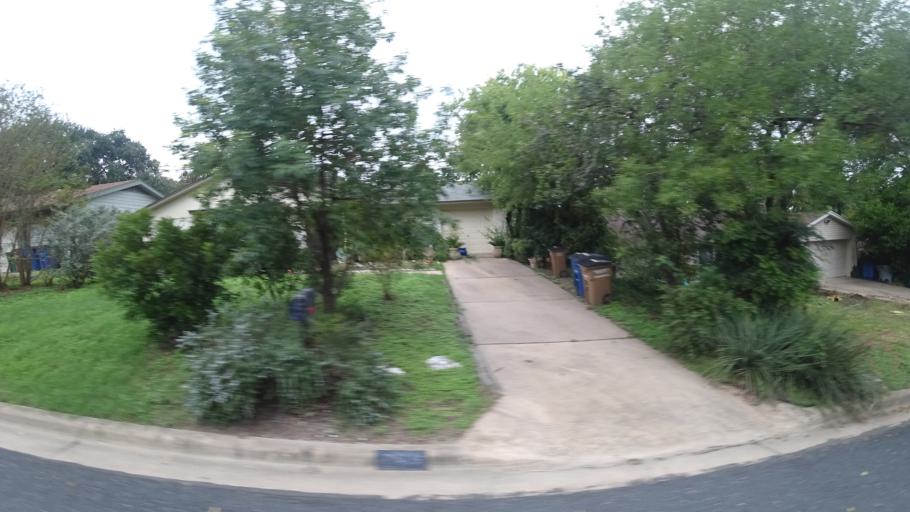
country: US
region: Texas
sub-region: Travis County
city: Austin
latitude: 30.3479
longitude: -97.6926
